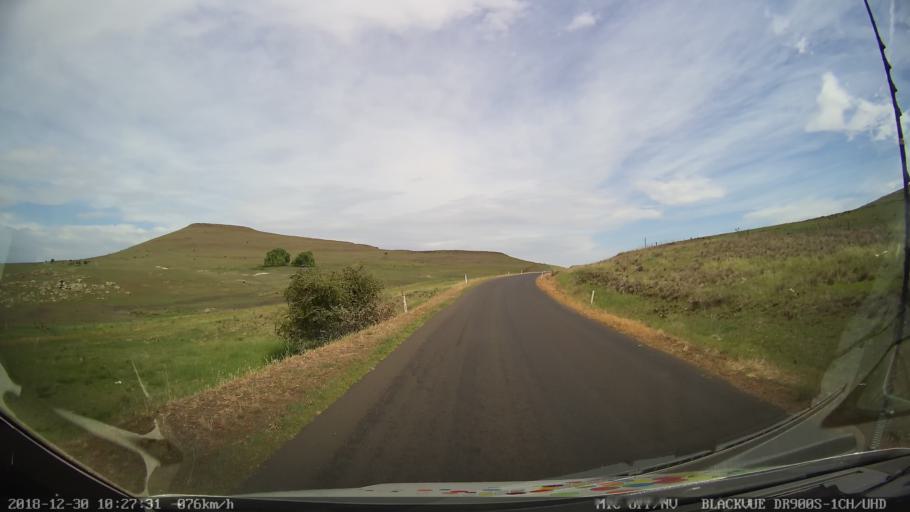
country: AU
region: New South Wales
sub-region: Snowy River
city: Berridale
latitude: -36.5127
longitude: 148.9312
